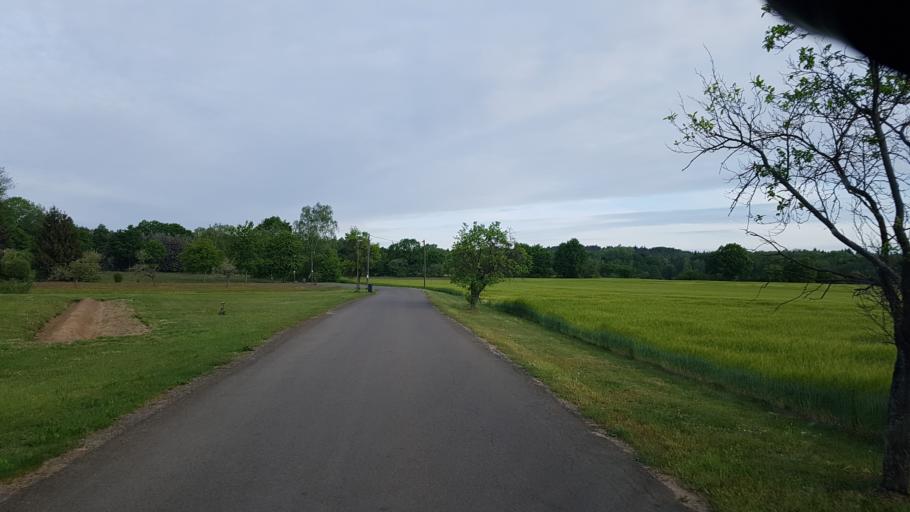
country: DE
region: Brandenburg
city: Luckau
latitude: 51.8066
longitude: 13.6398
